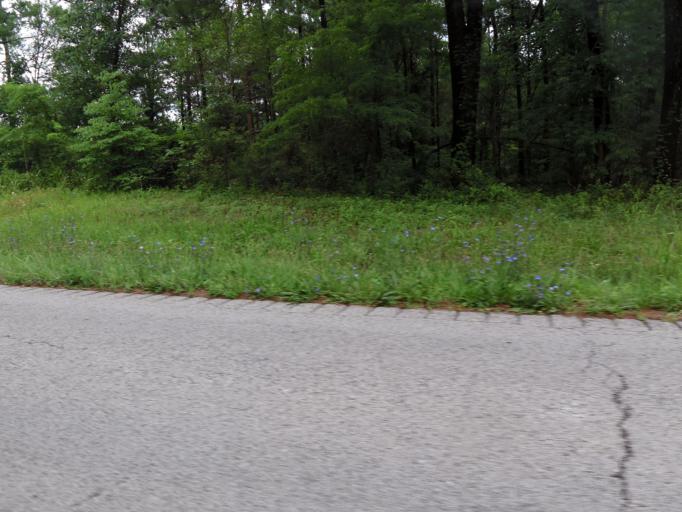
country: US
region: Kentucky
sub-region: Muhlenberg County
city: Morehead
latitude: 37.3017
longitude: -87.3342
